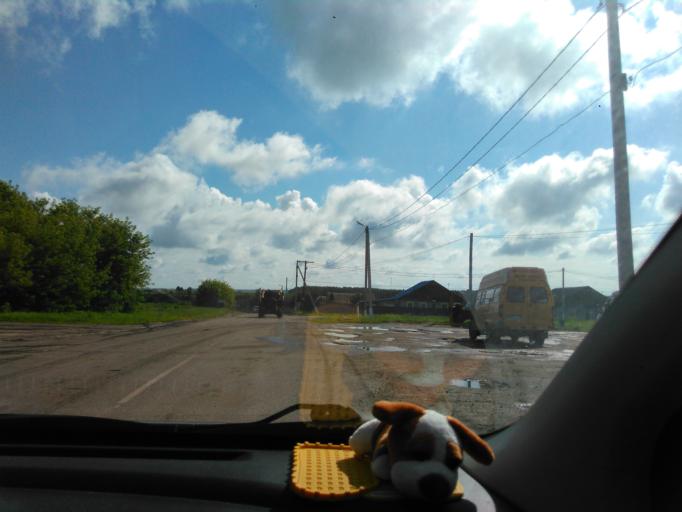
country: RU
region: Penza
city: Lermontovo
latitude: 53.1903
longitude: 44.0757
